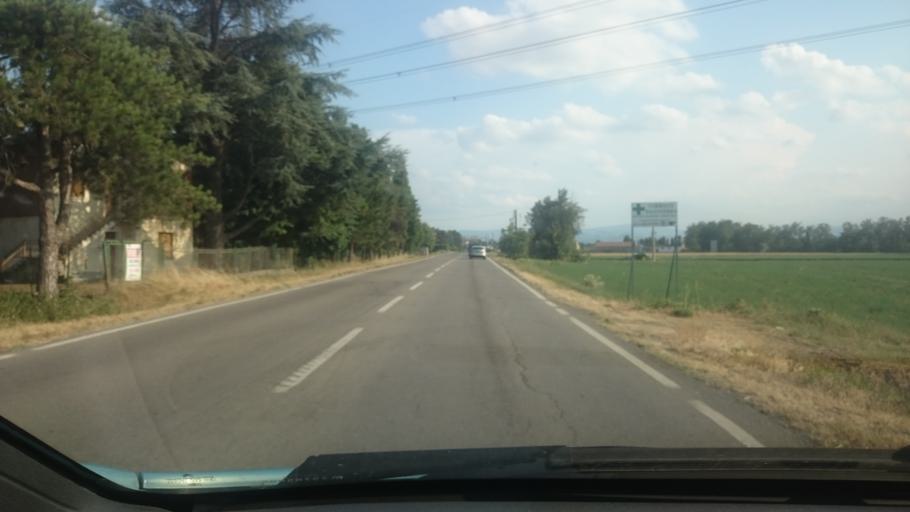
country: IT
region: Emilia-Romagna
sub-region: Provincia di Reggio Emilia
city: Salvaterra
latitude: 44.6204
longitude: 10.7777
